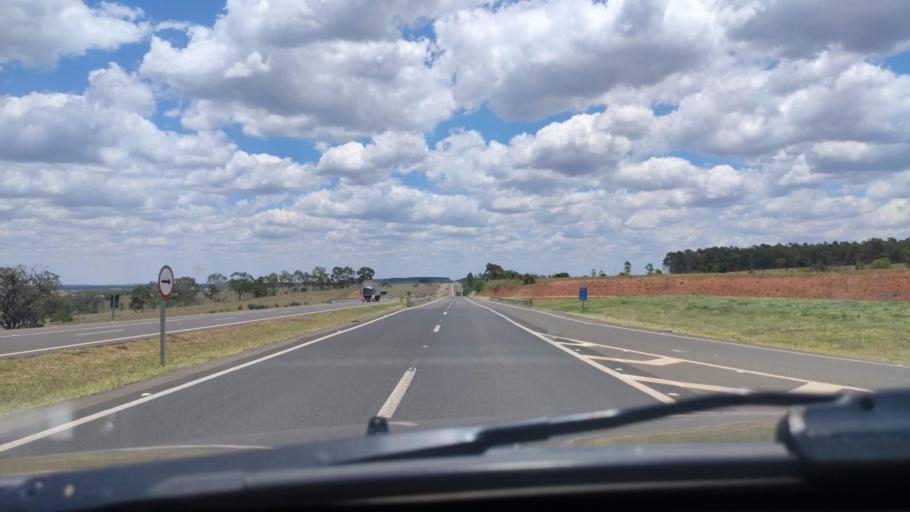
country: BR
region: Sao Paulo
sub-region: Duartina
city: Duartina
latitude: -22.4958
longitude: -49.2632
